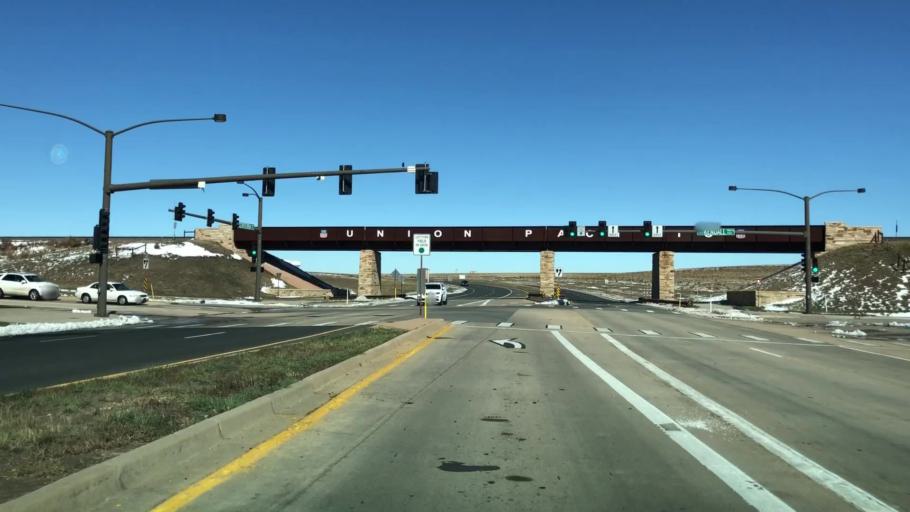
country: US
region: Colorado
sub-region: Larimer County
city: Loveland
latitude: 40.4159
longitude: -104.9855
